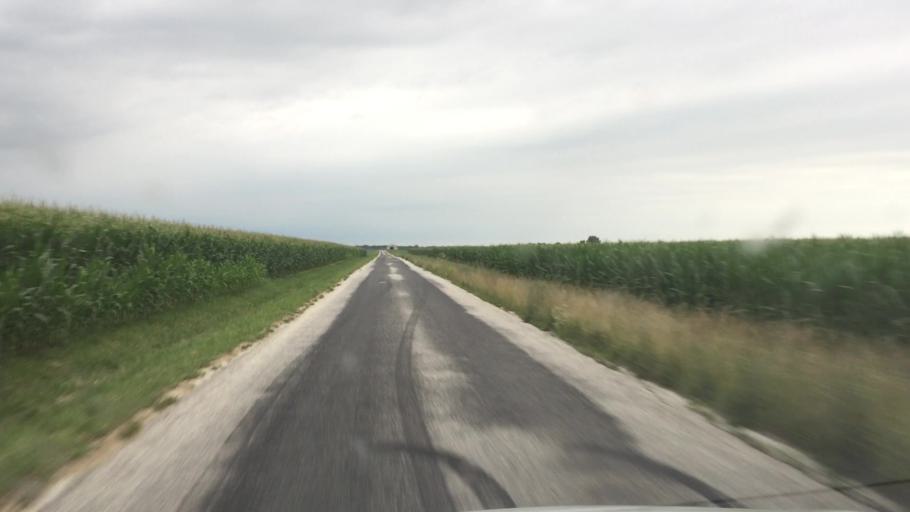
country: US
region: Illinois
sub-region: Adams County
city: Camp Point
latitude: 40.2203
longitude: -90.9691
